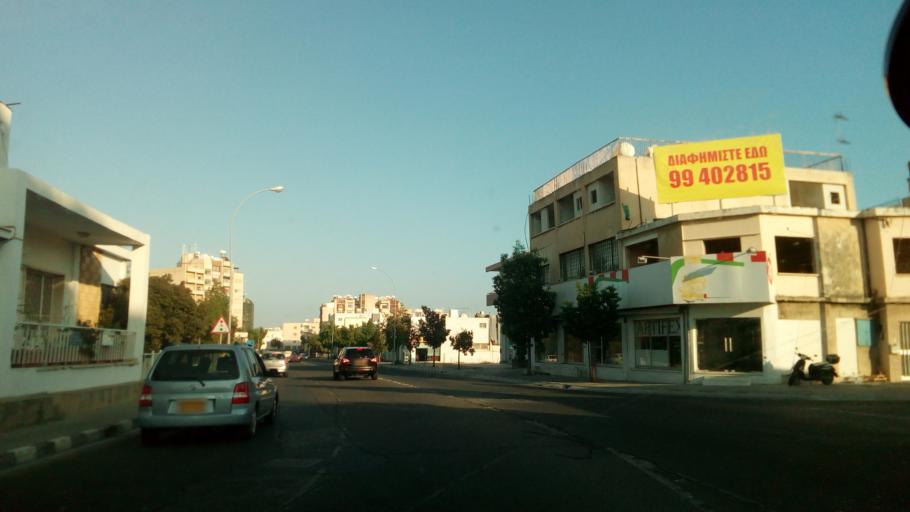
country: CY
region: Limassol
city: Limassol
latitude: 34.6888
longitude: 33.0188
